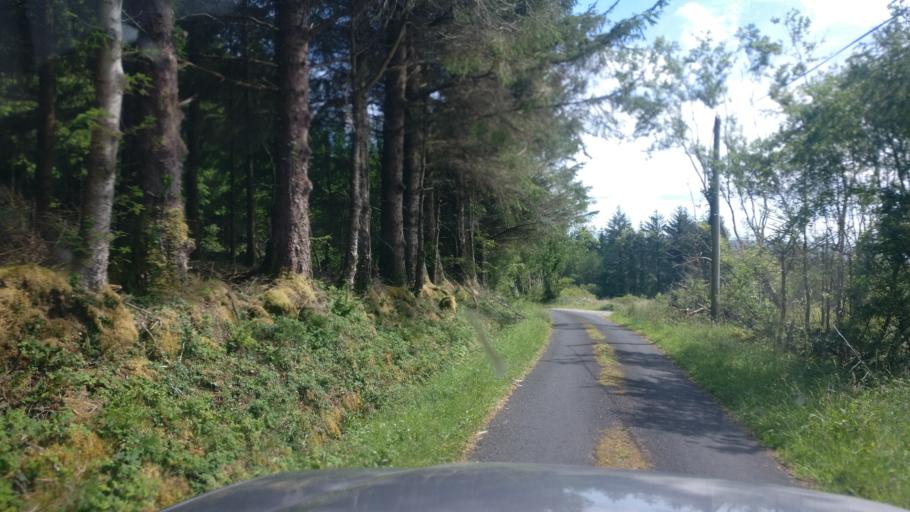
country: IE
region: Connaught
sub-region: County Galway
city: Gort
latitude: 53.0599
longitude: -8.6984
